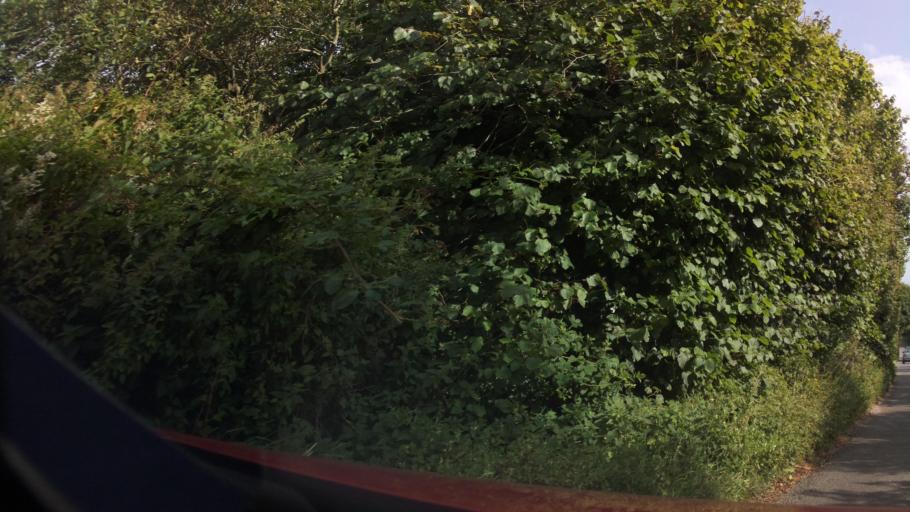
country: GB
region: England
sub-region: Hampshire
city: Milford on Sea
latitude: 50.7342
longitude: -1.6289
